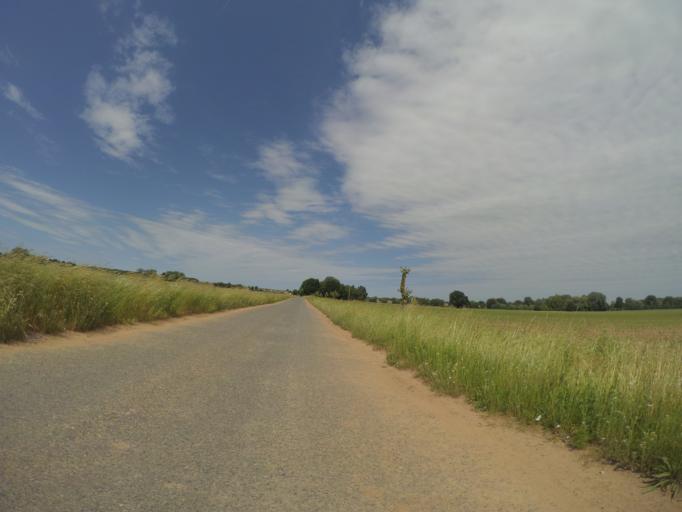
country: CZ
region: Central Bohemia
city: Milovice
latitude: 50.1734
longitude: 14.8857
